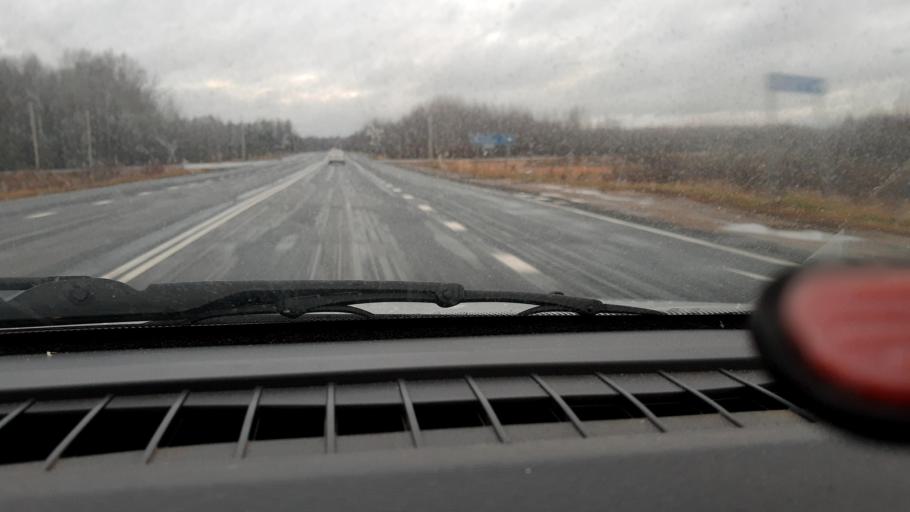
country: RU
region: Nizjnij Novgorod
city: Krasnyye Baki
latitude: 57.0963
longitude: 45.1624
